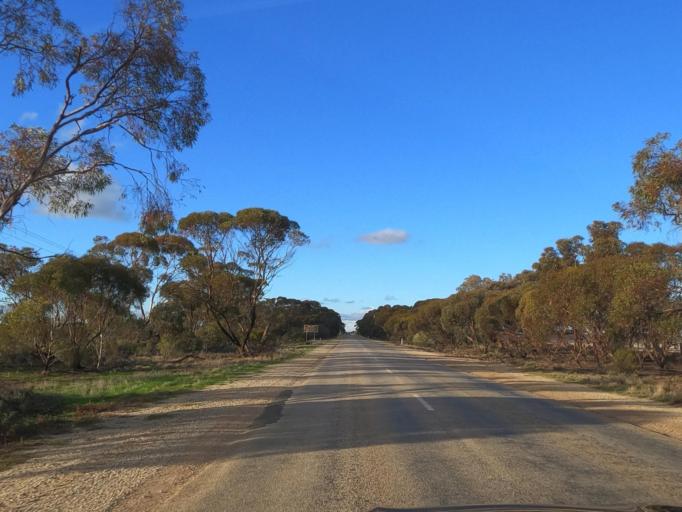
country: AU
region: Victoria
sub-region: Swan Hill
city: Swan Hill
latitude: -35.3476
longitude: 143.5178
